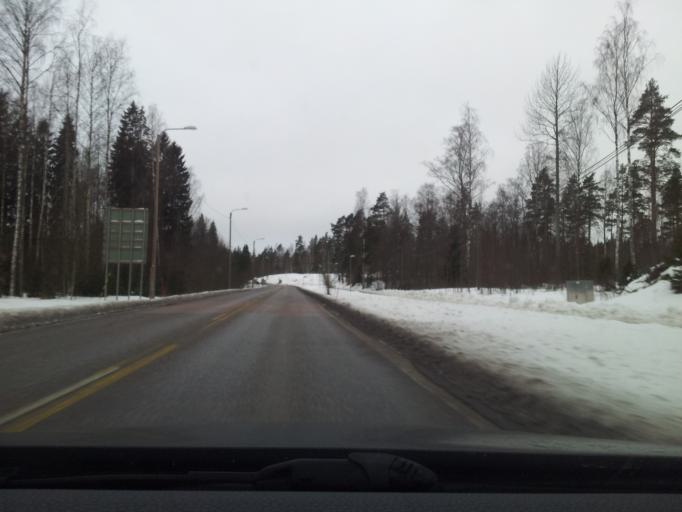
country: FI
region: Uusimaa
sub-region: Helsinki
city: Espoo
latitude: 60.1488
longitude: 24.5688
